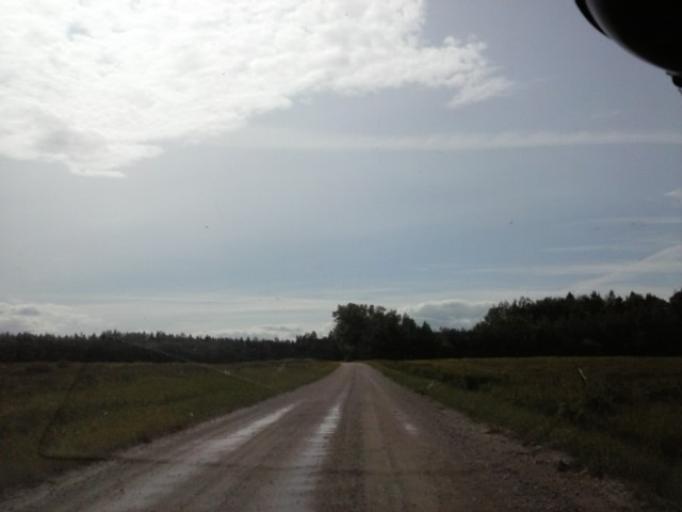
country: EE
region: Polvamaa
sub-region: Polva linn
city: Polva
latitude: 58.2522
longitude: 26.9751
